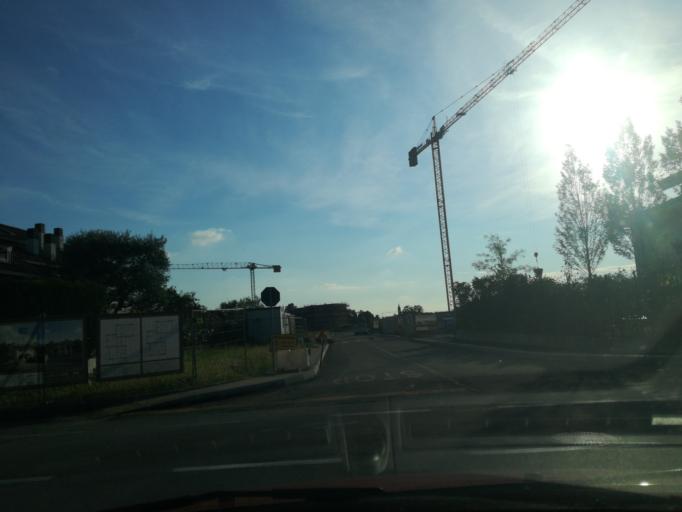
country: IT
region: Lombardy
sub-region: Provincia di Monza e Brianza
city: Bernareggio
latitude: 45.6458
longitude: 9.3980
